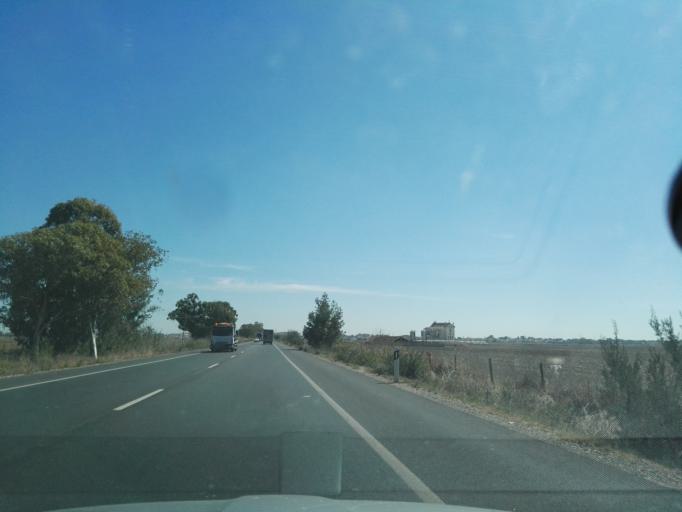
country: PT
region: Santarem
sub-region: Benavente
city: Samora Correia
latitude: 38.9298
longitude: -8.9072
